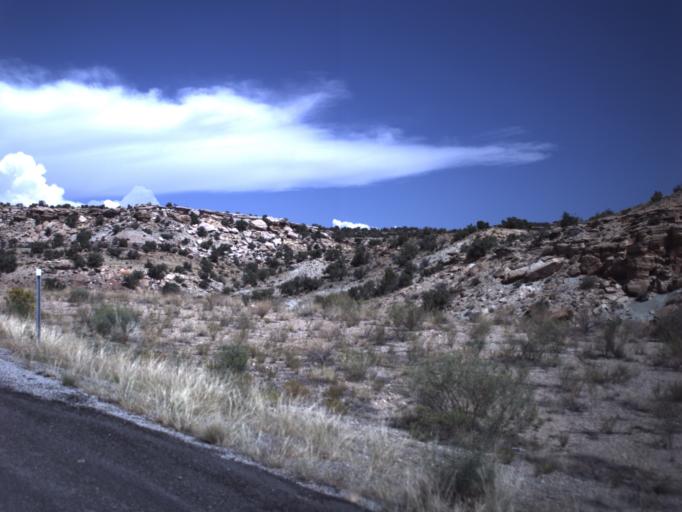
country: US
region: Utah
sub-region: San Juan County
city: Blanding
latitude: 37.4299
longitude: -109.4713
